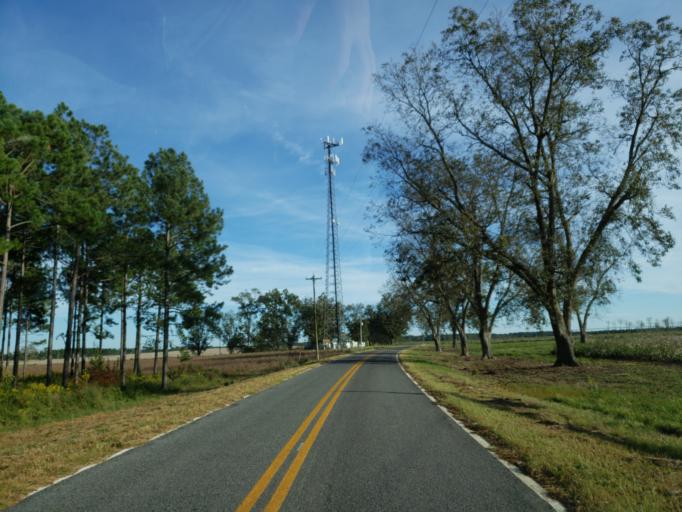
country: US
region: Georgia
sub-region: Dooly County
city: Vienna
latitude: 32.0718
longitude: -83.7806
